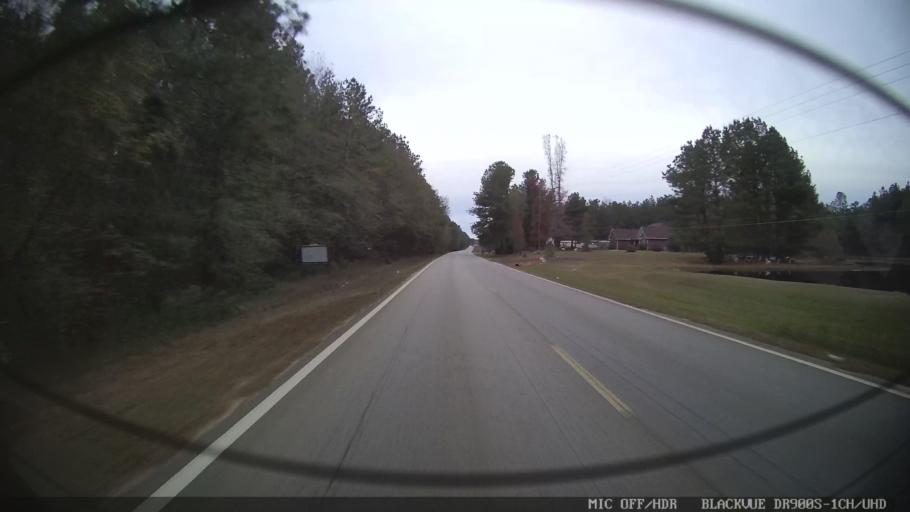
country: US
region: Mississippi
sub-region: Clarke County
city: Stonewall
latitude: 32.0488
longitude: -88.8943
